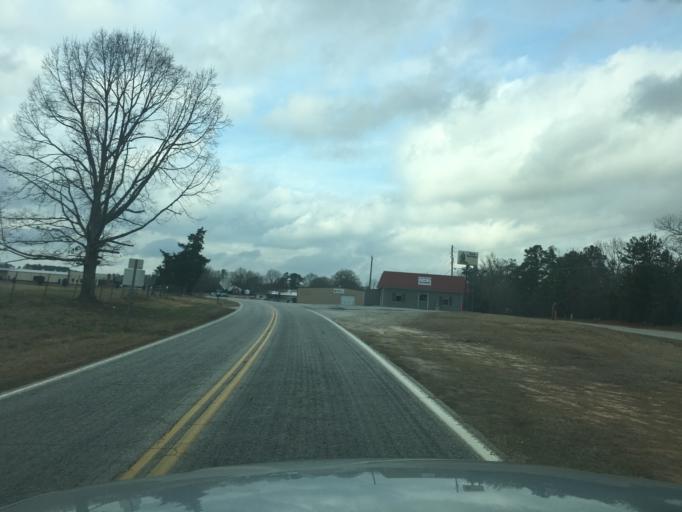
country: US
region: South Carolina
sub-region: Abbeville County
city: Abbeville
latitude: 34.2264
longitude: -82.3894
